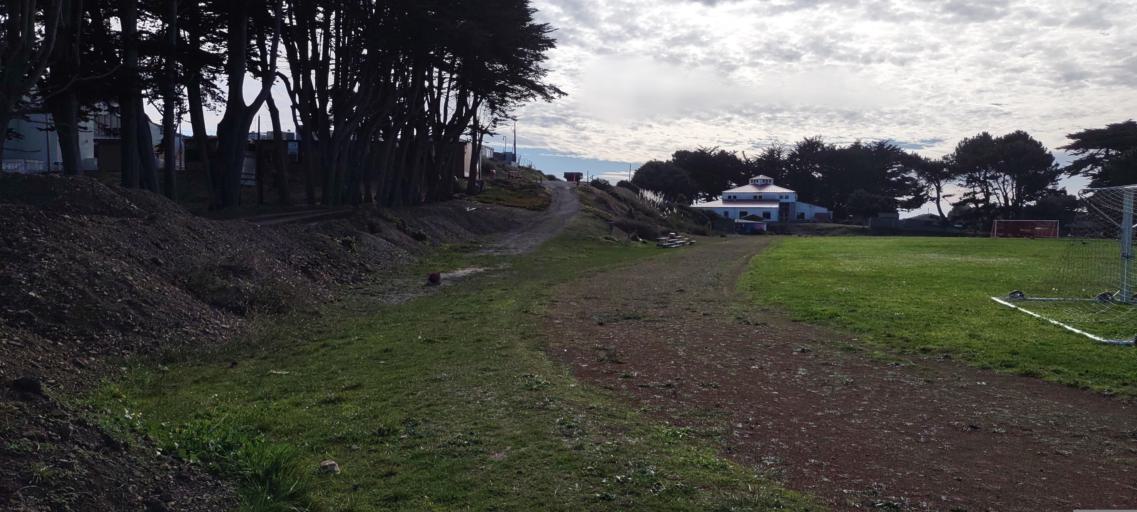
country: US
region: California
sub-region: Mendocino County
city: Fort Bragg
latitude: 39.3094
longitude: -123.8031
